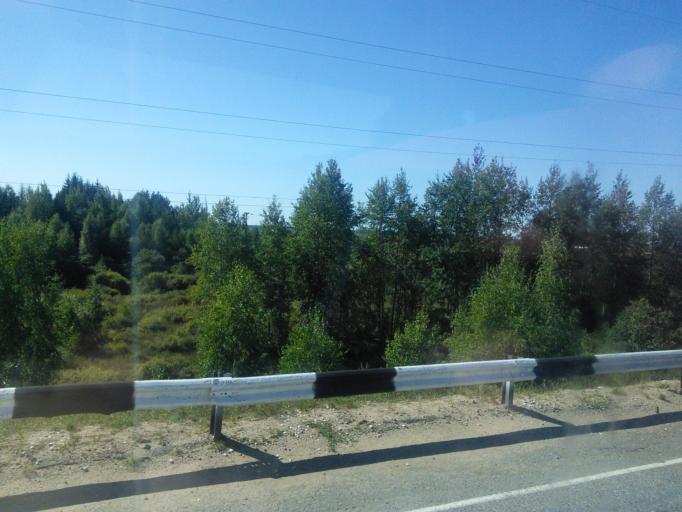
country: RU
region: Tverskaya
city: Kalyazin
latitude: 57.2328
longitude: 37.7914
